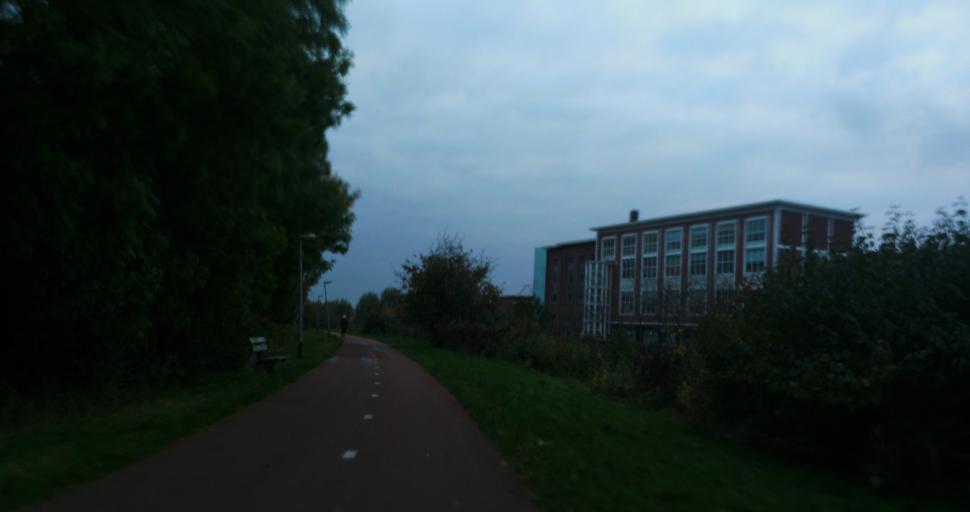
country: NL
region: Groningen
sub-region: Gemeente Groningen
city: Korrewegwijk
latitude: 53.2317
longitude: 6.5331
